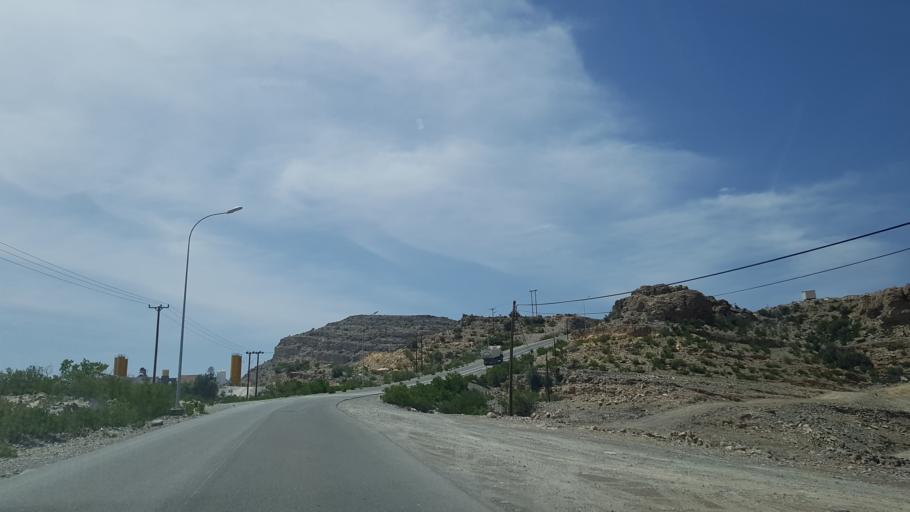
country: OM
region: Muhafazat ad Dakhiliyah
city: Izki
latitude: 23.1010
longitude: 57.6702
